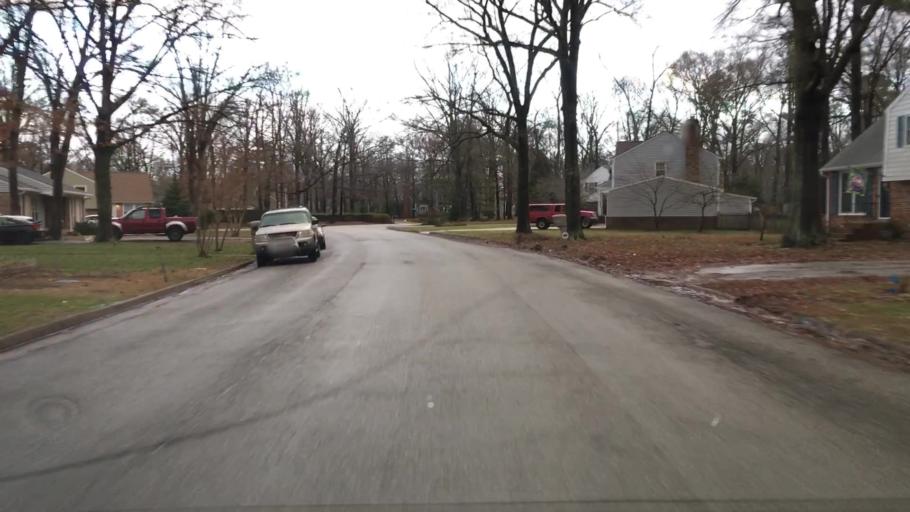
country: US
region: Virginia
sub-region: Chesterfield County
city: Bon Air
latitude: 37.5145
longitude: -77.6213
